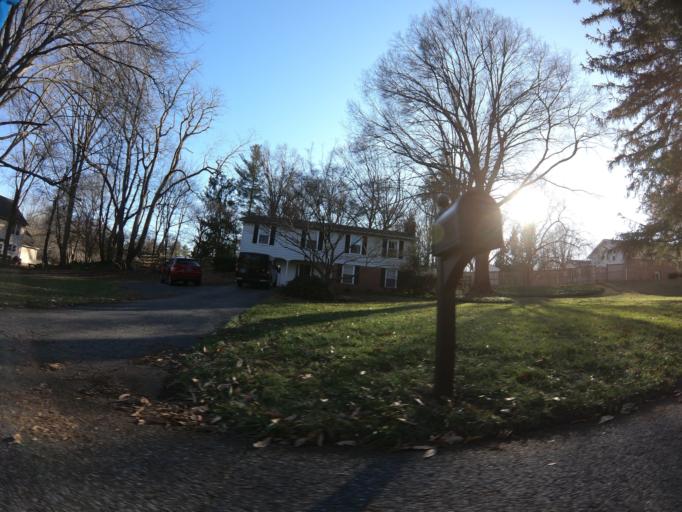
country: US
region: Maryland
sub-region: Howard County
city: Columbia
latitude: 39.2488
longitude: -76.8620
